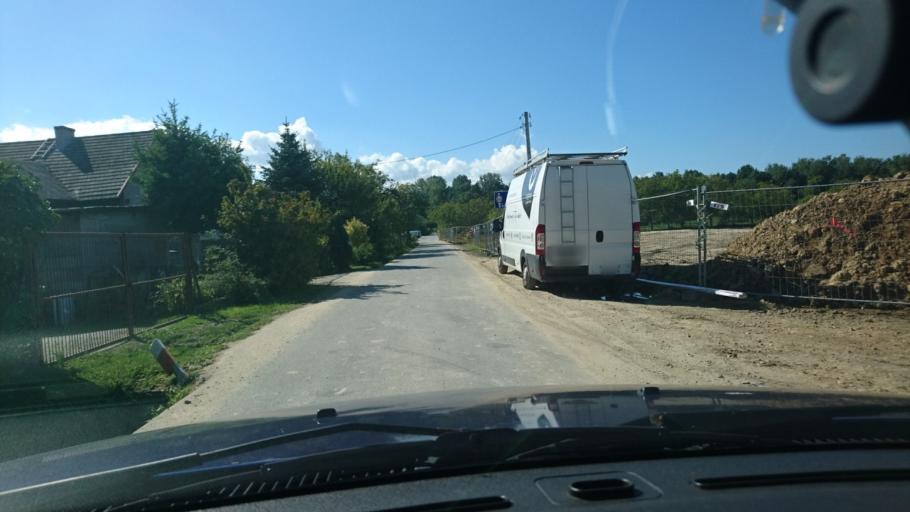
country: PL
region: Silesian Voivodeship
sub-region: Powiat bielski
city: Jaworze
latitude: 49.8206
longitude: 18.9676
